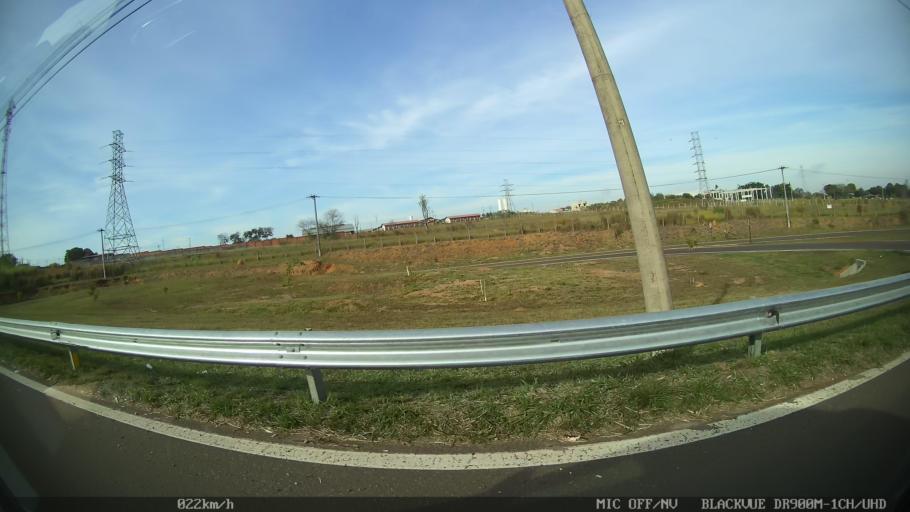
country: BR
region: Sao Paulo
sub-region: Piracicaba
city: Piracicaba
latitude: -22.6788
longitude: -47.7151
